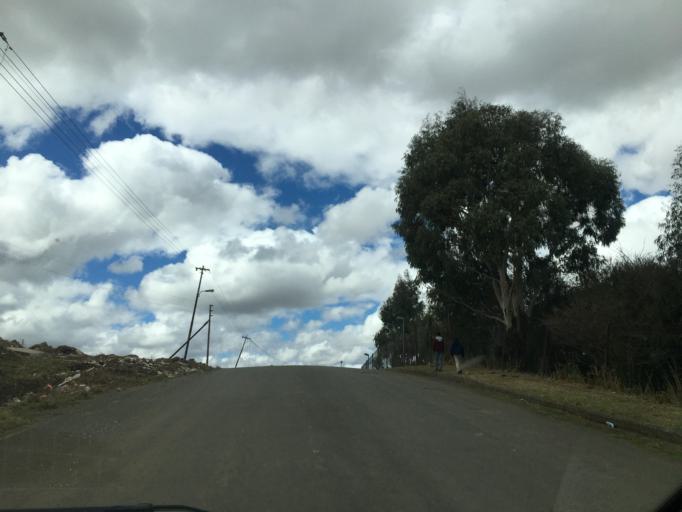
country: ZA
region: Eastern Cape
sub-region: Chris Hani District Municipality
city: Elliot
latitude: -31.3311
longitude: 27.8486
